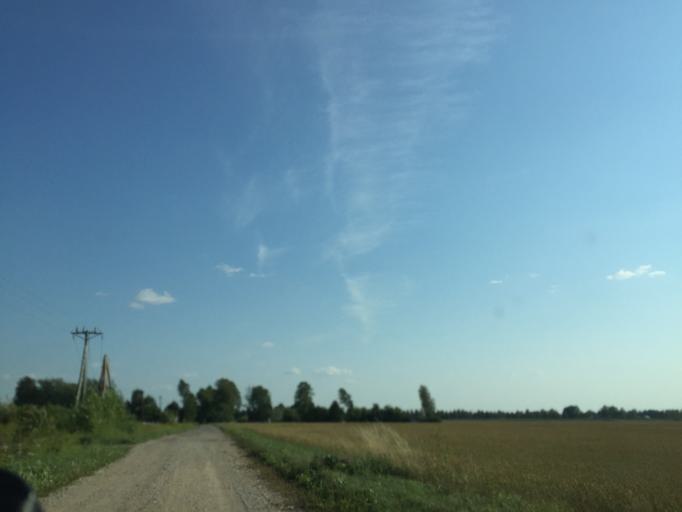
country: LV
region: Jelgava
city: Jelgava
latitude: 56.4565
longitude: 23.6809
